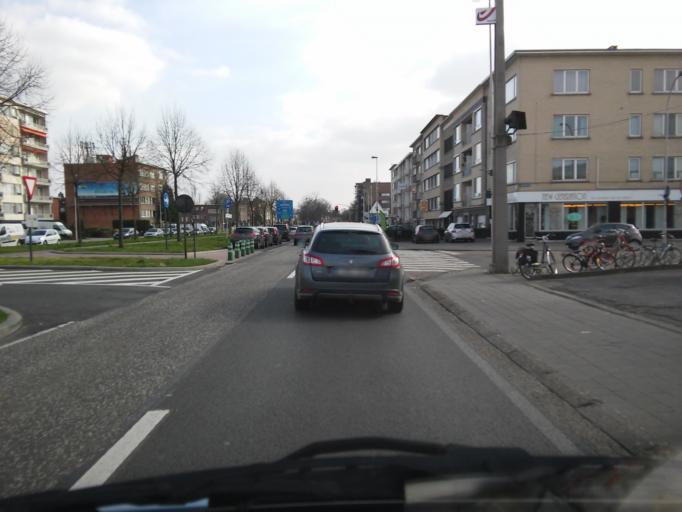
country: BE
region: Flanders
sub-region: Provincie Antwerpen
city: Edegem
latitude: 51.1750
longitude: 4.4250
